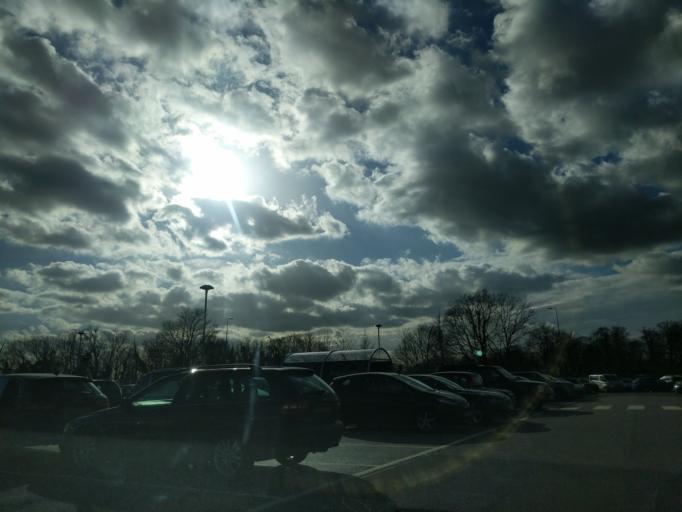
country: GB
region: England
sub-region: Central Bedfordshire
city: Biggleswade
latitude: 52.0741
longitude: -0.2449
